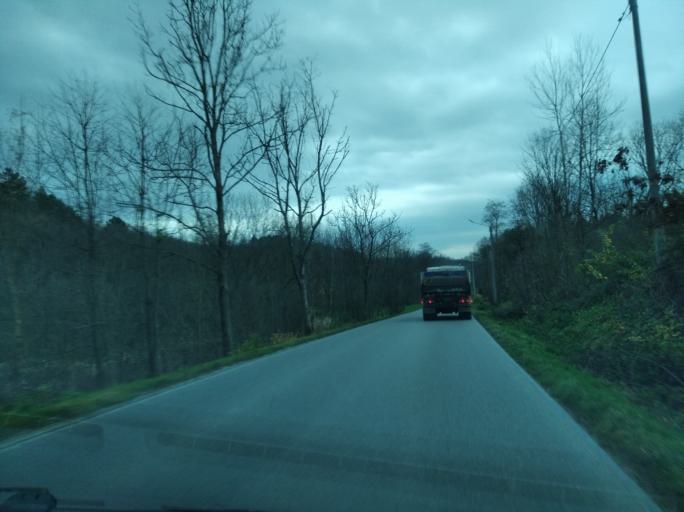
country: PL
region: Subcarpathian Voivodeship
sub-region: Powiat strzyzowski
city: Wisniowa
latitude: 49.9311
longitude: 21.7106
